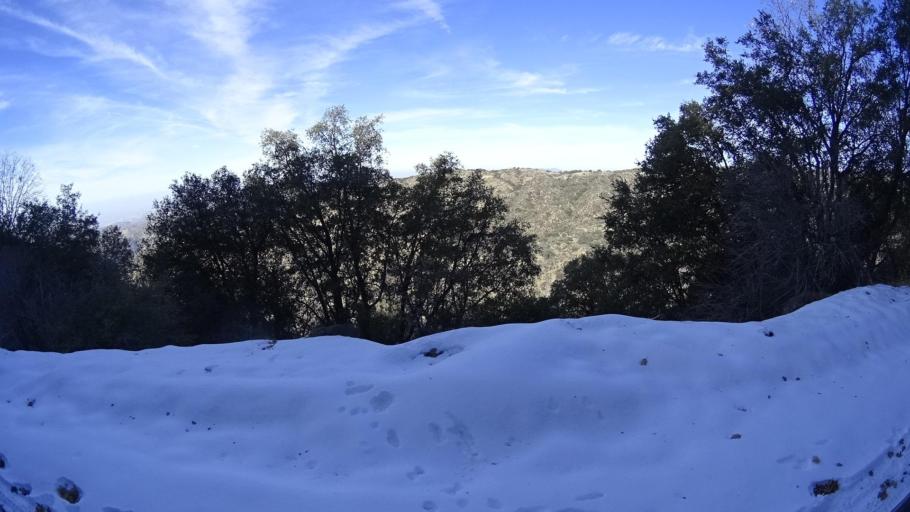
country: US
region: California
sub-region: Kern County
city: Bodfish
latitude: 35.4773
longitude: -118.6449
